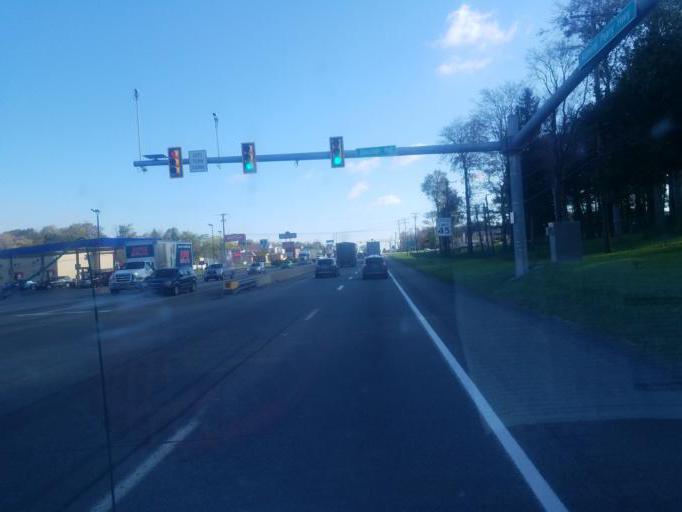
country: US
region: Pennsylvania
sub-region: Cambria County
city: Ebensburg
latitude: 40.4708
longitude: -78.7520
